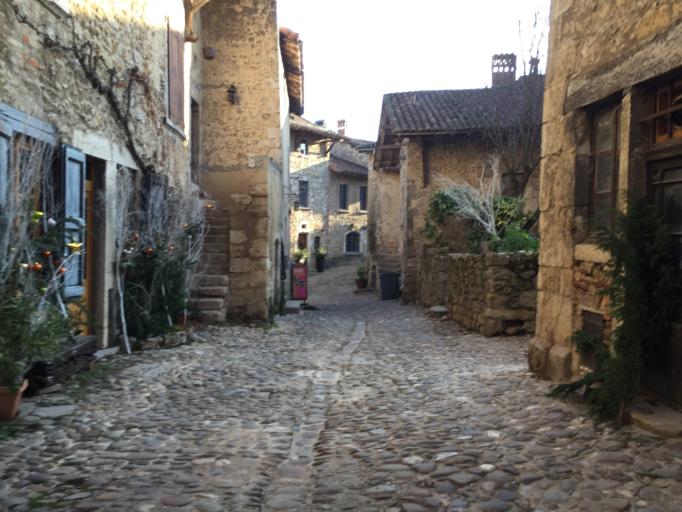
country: FR
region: Rhone-Alpes
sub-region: Departement de l'Ain
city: Perouges
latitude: 45.9033
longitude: 5.1805
